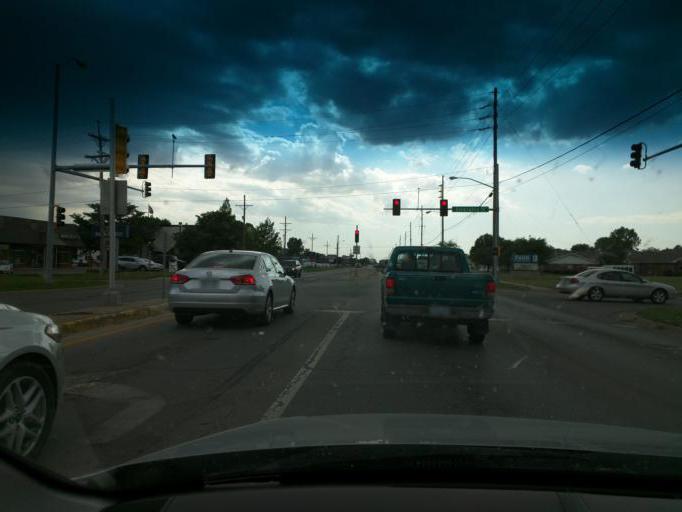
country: US
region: Kansas
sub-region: Reno County
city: Hutchinson
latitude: 38.0866
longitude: -97.9127
